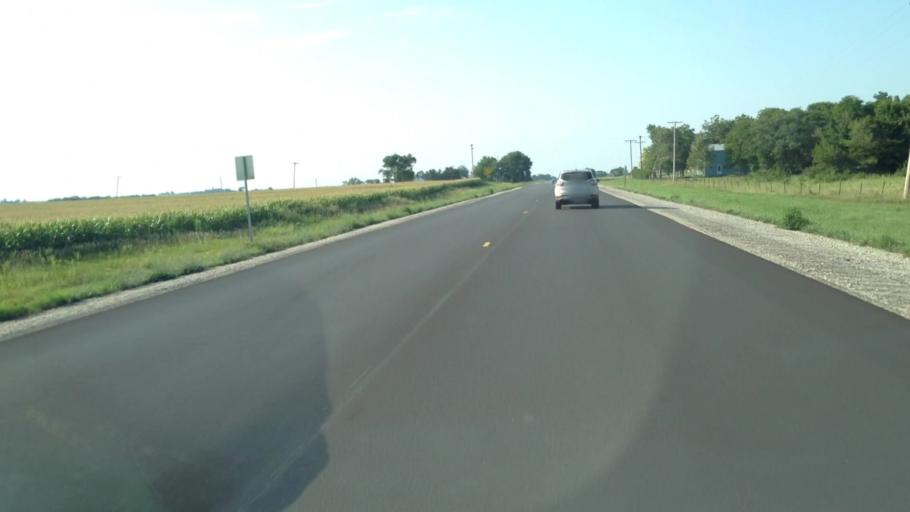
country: US
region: Kansas
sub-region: Anderson County
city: Garnett
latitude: 38.3658
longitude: -95.2488
